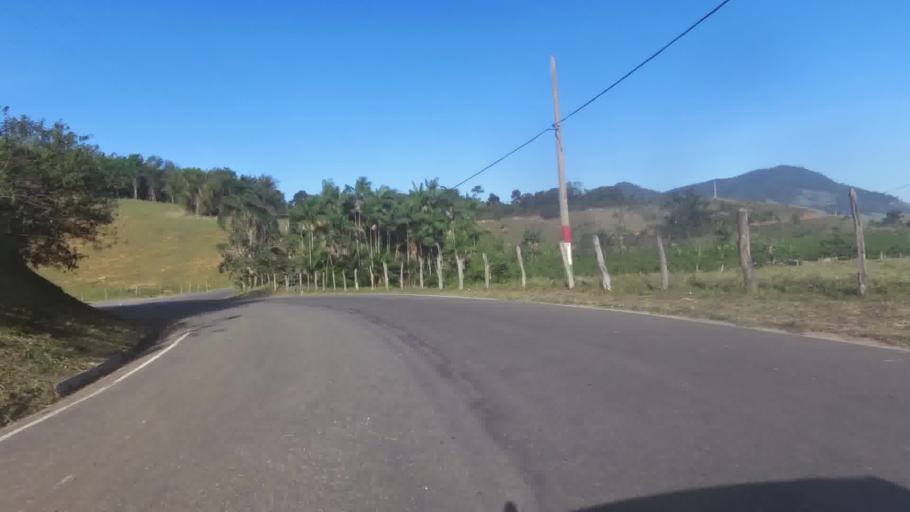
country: BR
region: Espirito Santo
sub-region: Iconha
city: Iconha
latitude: -20.7328
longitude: -40.7701
